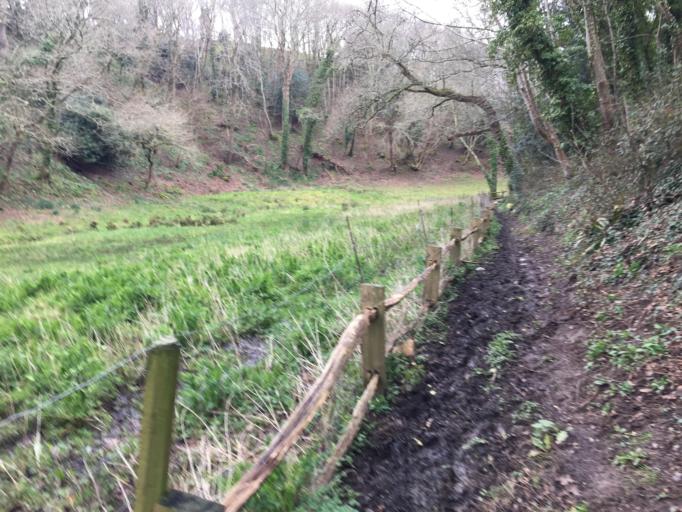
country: JE
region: St Helier
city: Saint Helier
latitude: 49.2147
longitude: -2.1333
